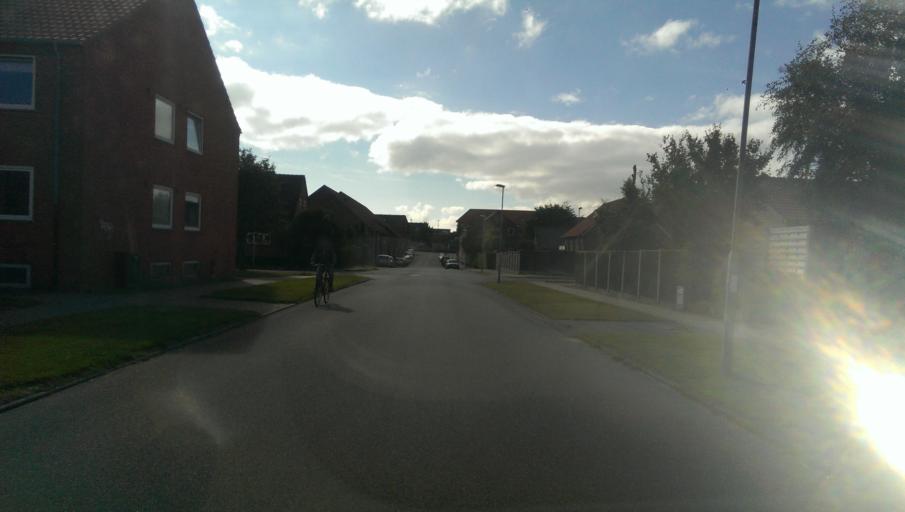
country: DK
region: South Denmark
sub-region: Esbjerg Kommune
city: Esbjerg
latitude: 55.4695
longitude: 8.4643
